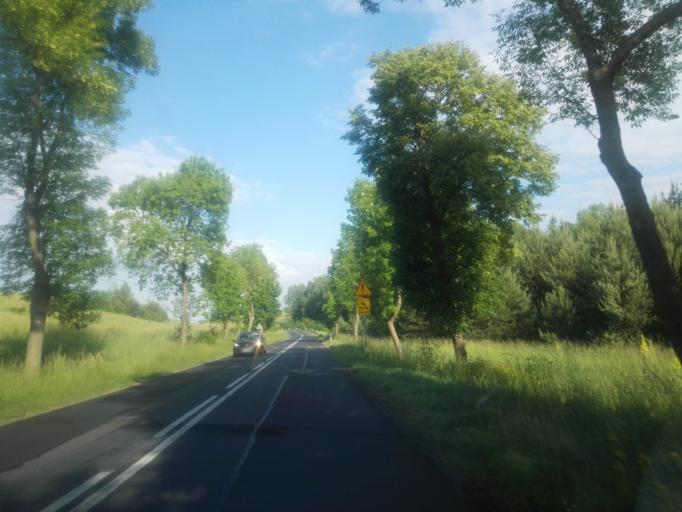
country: PL
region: Silesian Voivodeship
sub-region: Powiat czestochowski
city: Potok Zloty
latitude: 50.7368
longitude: 19.3678
